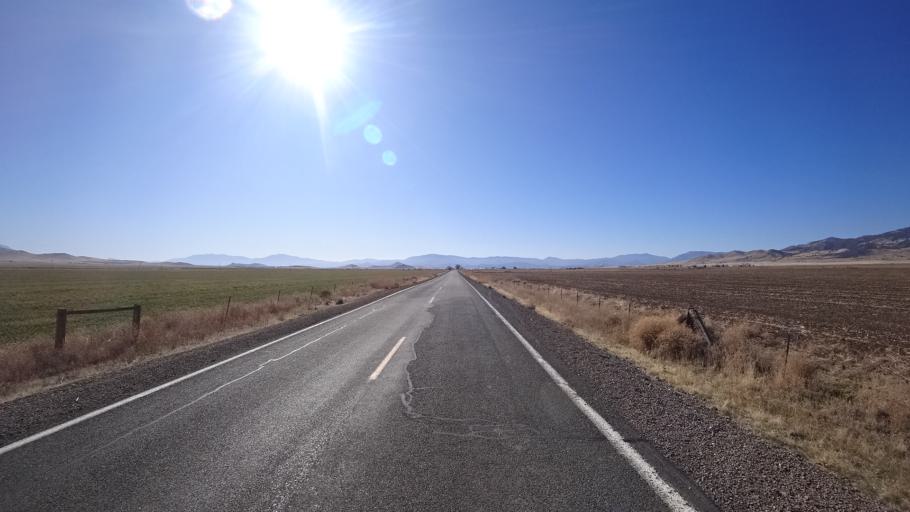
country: US
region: California
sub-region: Siskiyou County
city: Montague
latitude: 41.7980
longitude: -122.4513
